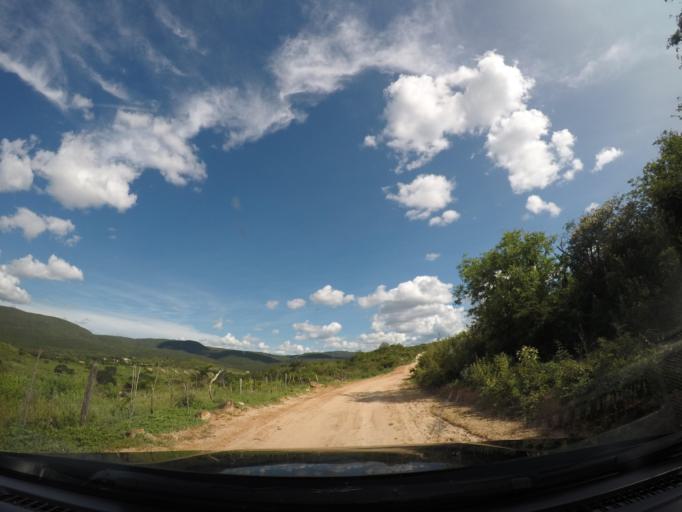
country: BR
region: Bahia
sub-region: Barra Da Estiva
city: Barra da Estiva
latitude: -13.1968
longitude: -41.5956
